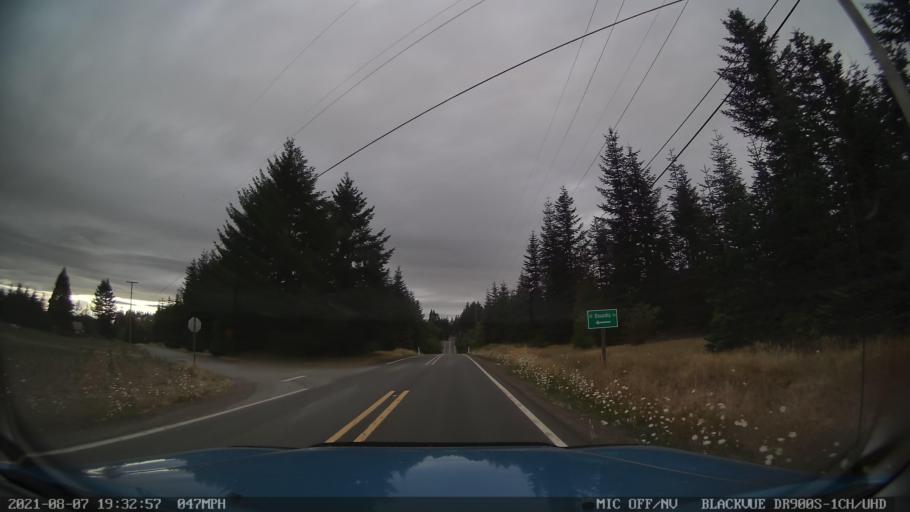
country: US
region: Oregon
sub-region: Linn County
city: Lyons
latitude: 44.9040
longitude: -122.6497
